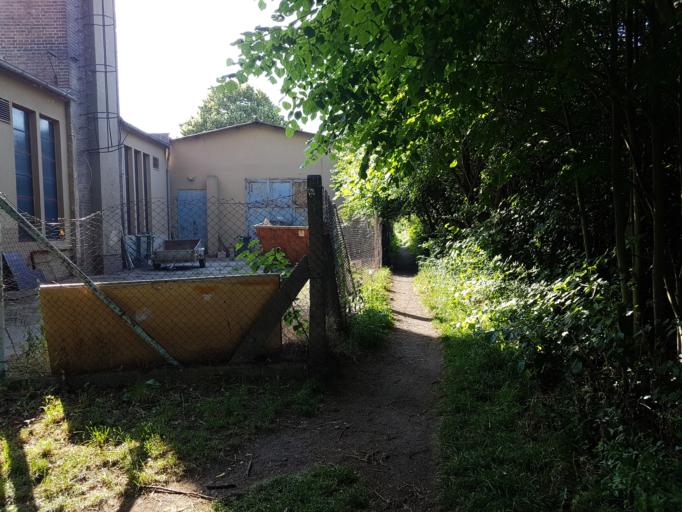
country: CZ
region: Central Bohemia
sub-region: Okres Nymburk
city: Podebrady
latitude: 50.1545
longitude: 15.1326
